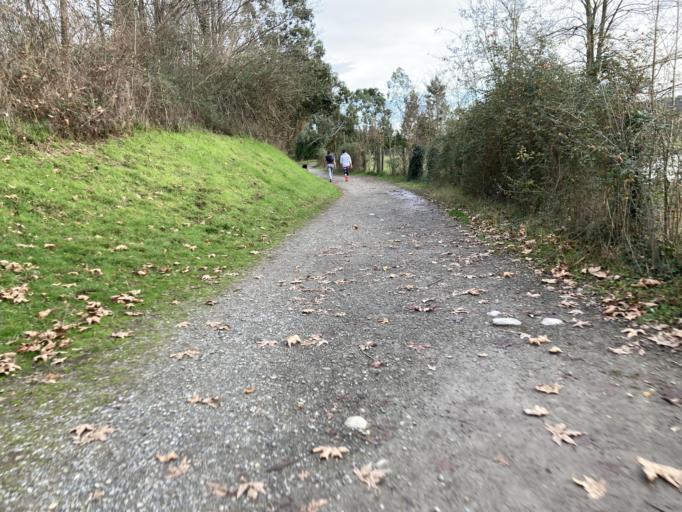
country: FR
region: Aquitaine
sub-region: Departement des Pyrenees-Atlantiques
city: Lescar
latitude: 43.3105
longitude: -0.4345
